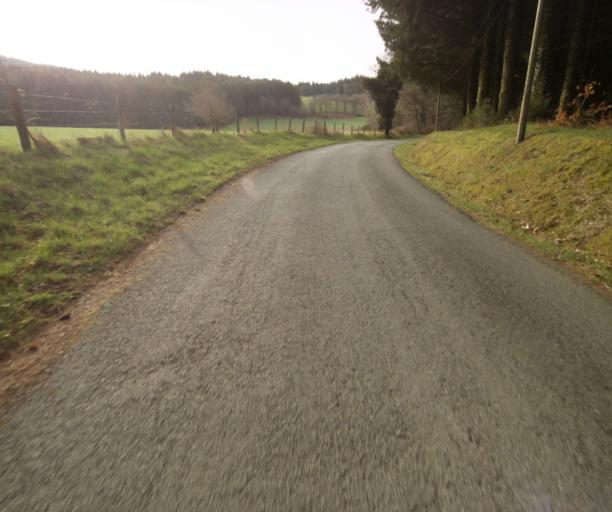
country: FR
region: Limousin
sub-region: Departement de la Correze
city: Treignac
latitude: 45.4662
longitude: 1.8112
